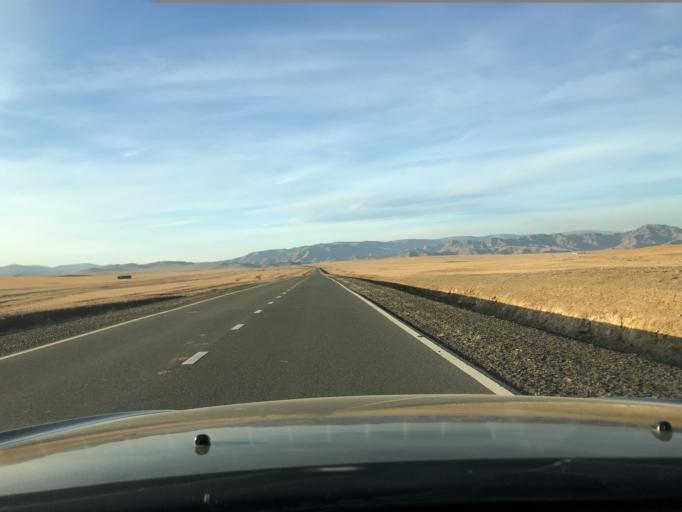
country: MN
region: Central Aimak
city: Arhust
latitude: 47.7437
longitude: 107.4590
